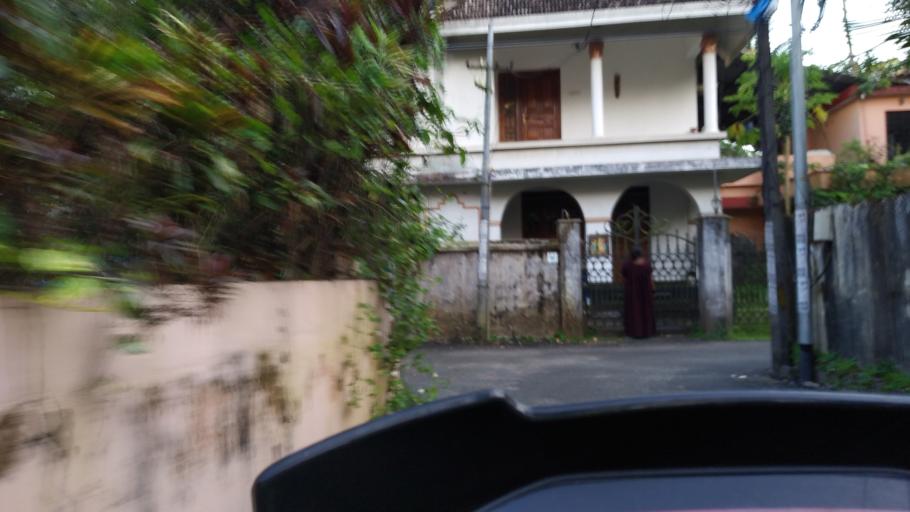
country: IN
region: Kerala
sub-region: Alappuzha
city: Arukutti
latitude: 9.9525
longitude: 76.3468
